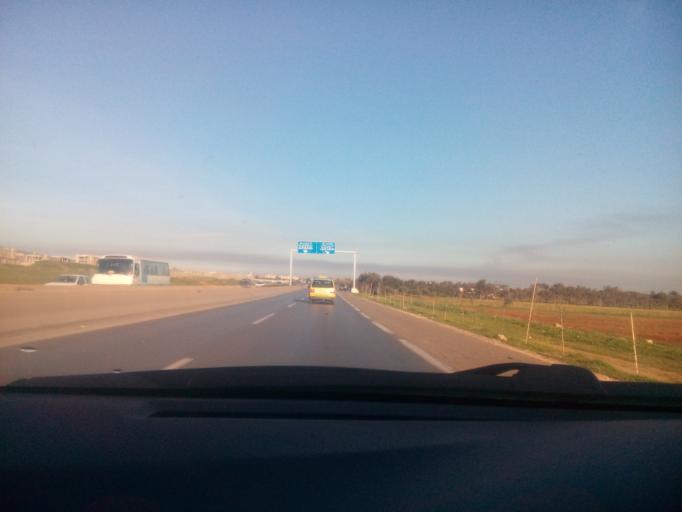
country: DZ
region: Oran
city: Bir el Djir
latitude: 35.7701
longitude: -0.4497
